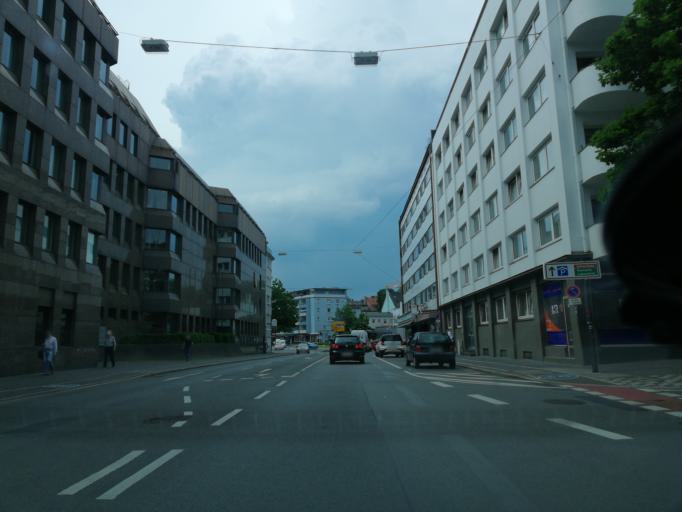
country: DE
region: North Rhine-Westphalia
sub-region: Regierungsbezirk Dusseldorf
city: Wuppertal
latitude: 51.2581
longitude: 7.1543
